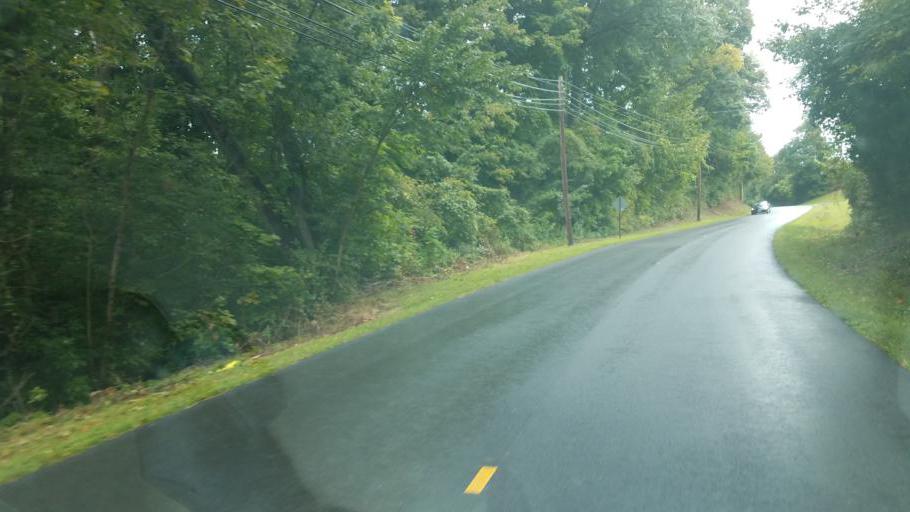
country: US
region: Ohio
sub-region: Scioto County
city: Lucasville
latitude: 38.8807
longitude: -82.9933
